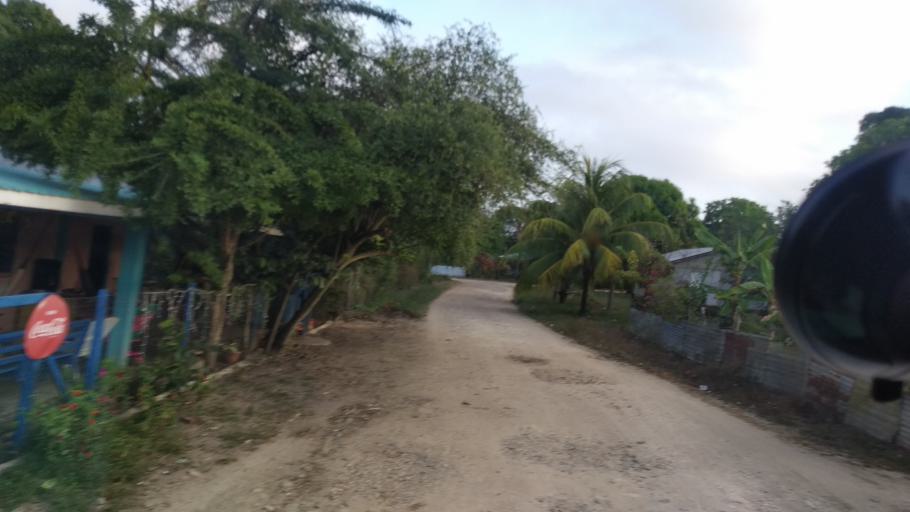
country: BZ
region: Stann Creek
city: Placencia
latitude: 16.5702
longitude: -88.5279
